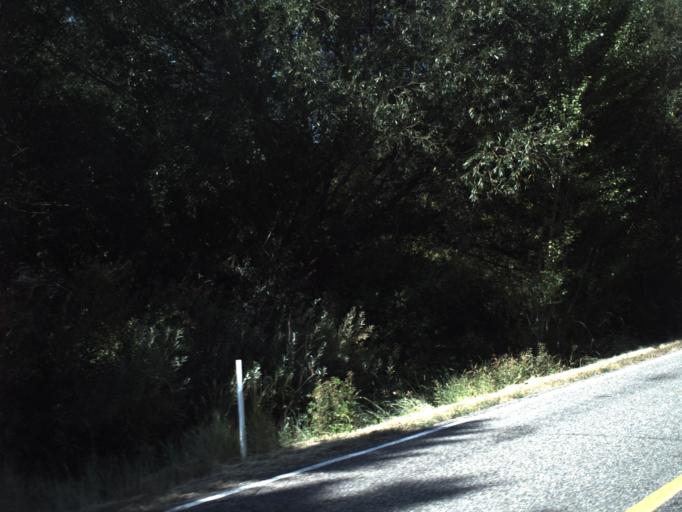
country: US
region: Utah
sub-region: Cache County
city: Millville
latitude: 41.6297
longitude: -111.7173
